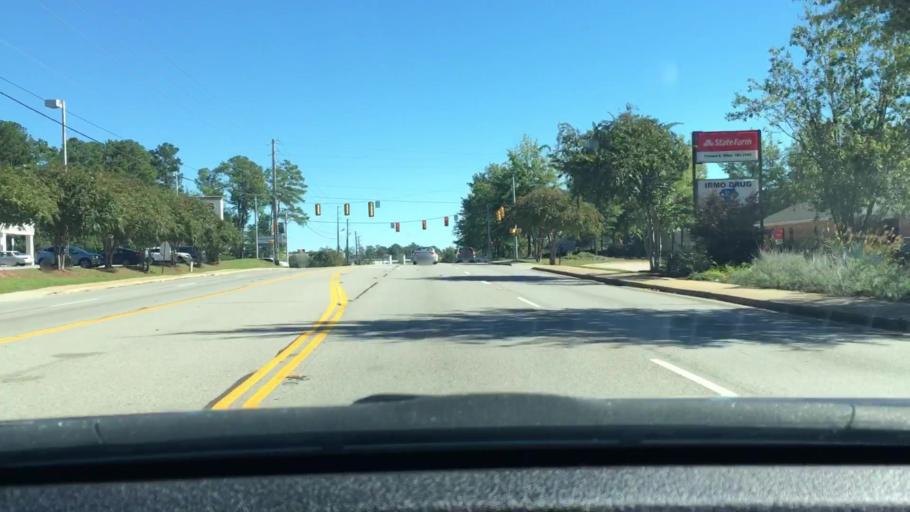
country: US
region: South Carolina
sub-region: Lexington County
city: Irmo
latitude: 34.0893
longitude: -81.1751
